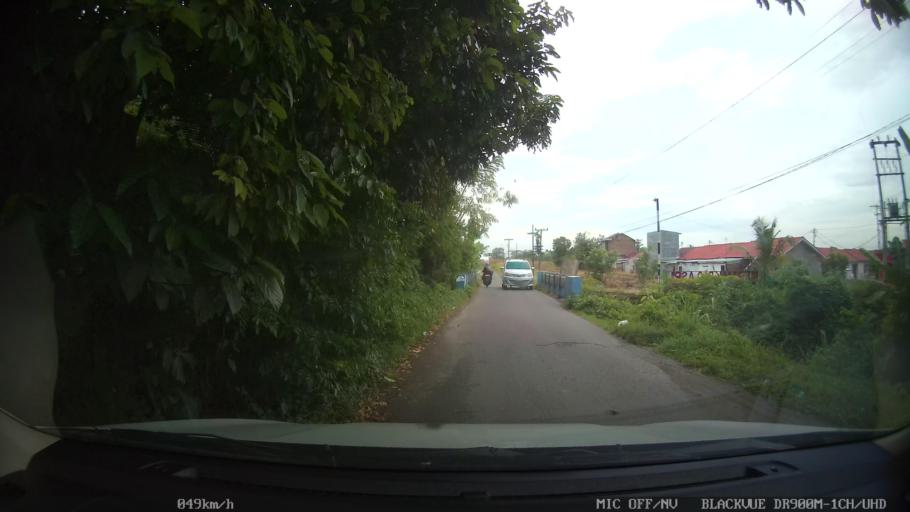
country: ID
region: North Sumatra
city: Sunggal
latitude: 3.5727
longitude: 98.5791
